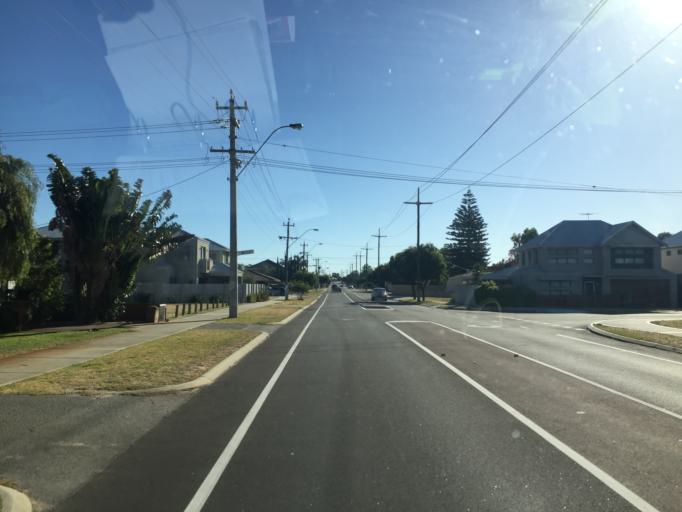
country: AU
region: Western Australia
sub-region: Belmont
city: Rivervale
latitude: -31.9634
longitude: 115.9253
